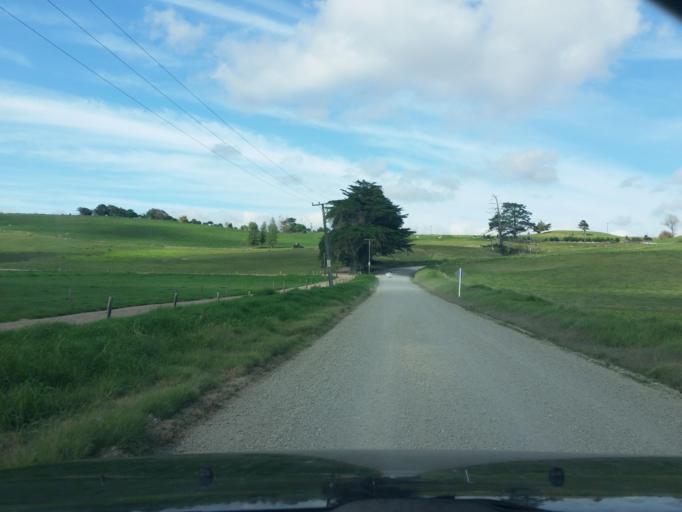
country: NZ
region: Northland
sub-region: Kaipara District
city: Dargaville
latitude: -36.0020
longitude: 173.9477
